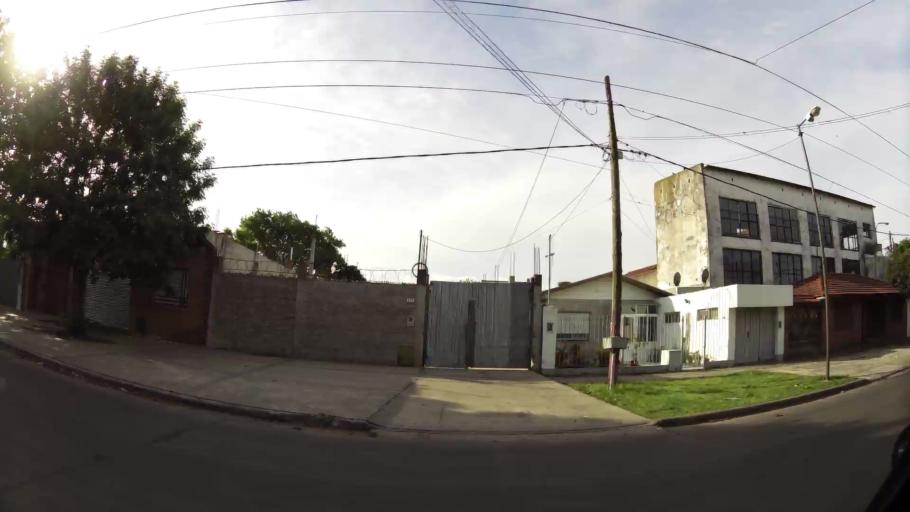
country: AR
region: Buenos Aires
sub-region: Partido de Quilmes
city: Quilmes
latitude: -34.7414
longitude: -58.2592
